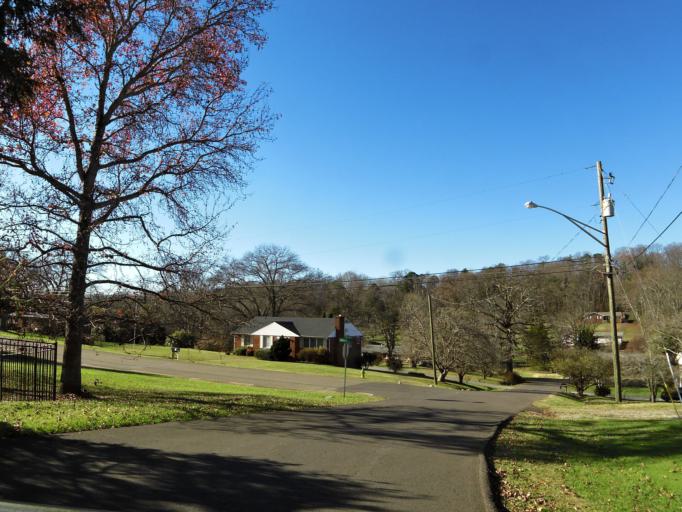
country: US
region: Tennessee
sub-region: Knox County
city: Knoxville
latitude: 36.0288
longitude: -83.9621
